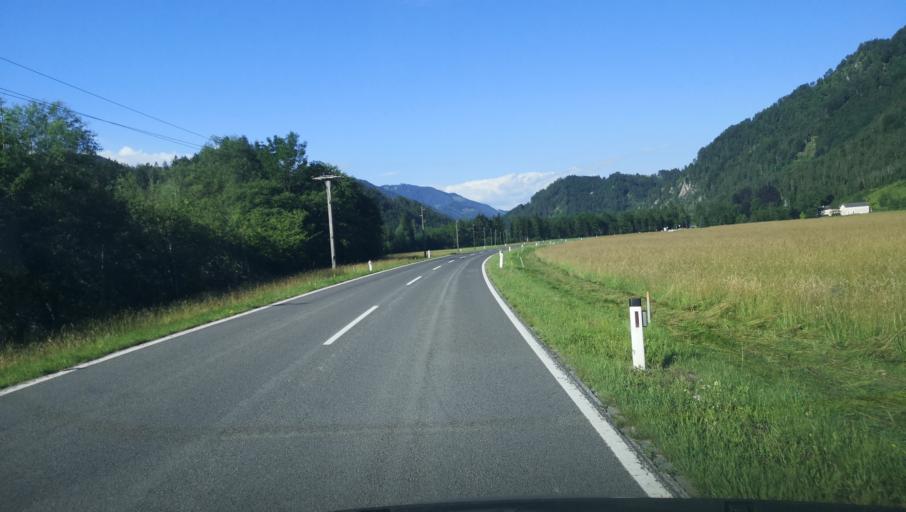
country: AT
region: Lower Austria
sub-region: Politischer Bezirk Amstetten
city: Opponitz
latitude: 47.8769
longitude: 14.8086
